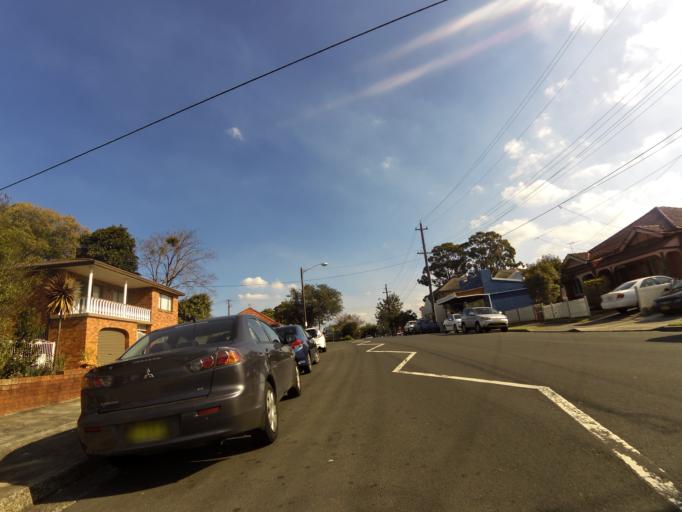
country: AU
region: New South Wales
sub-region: Hurstville
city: Penshurst
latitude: -33.9714
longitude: 151.0819
